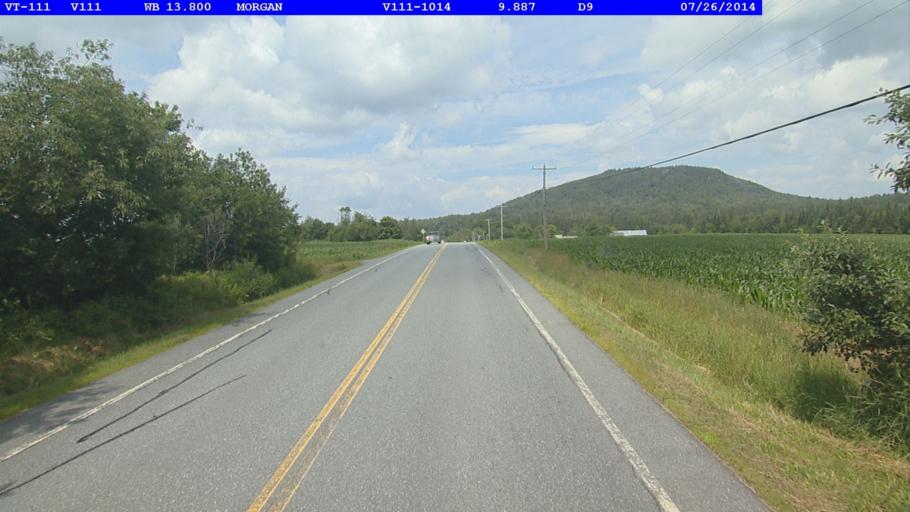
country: US
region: Vermont
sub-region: Orleans County
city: Newport
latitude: 44.8592
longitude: -71.9260
